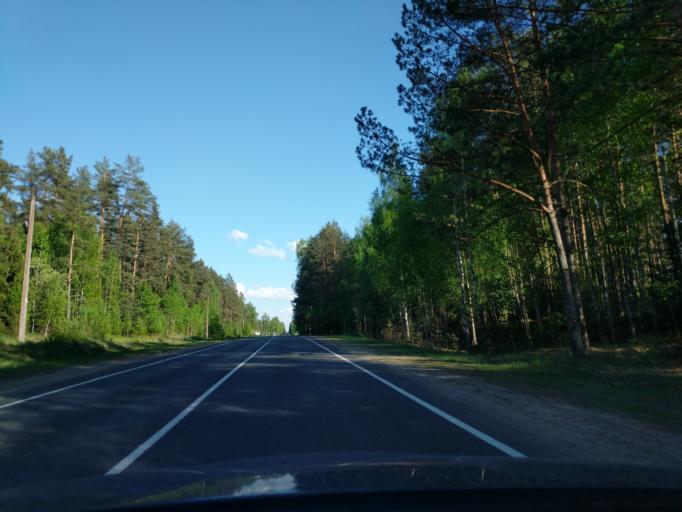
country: BY
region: Minsk
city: Myadzyel
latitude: 54.8176
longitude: 26.9649
